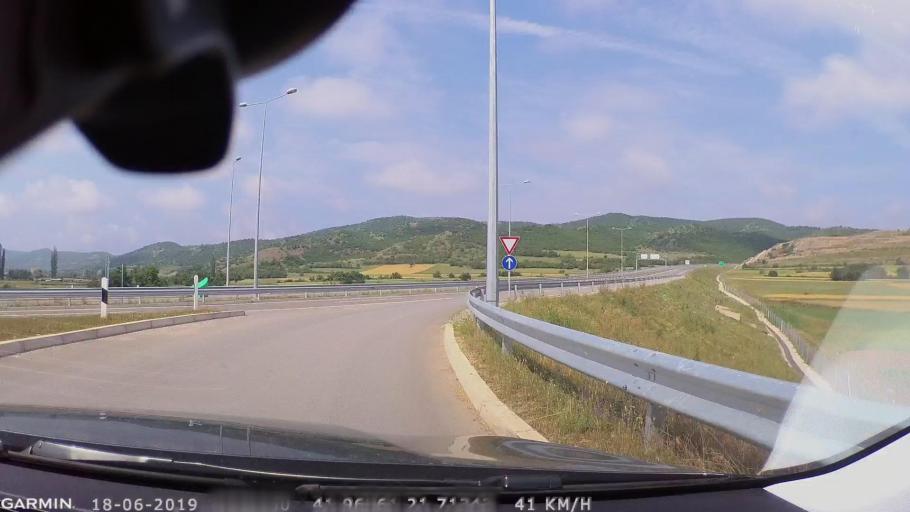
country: MK
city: Miladinovci
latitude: 41.9843
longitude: 21.6556
